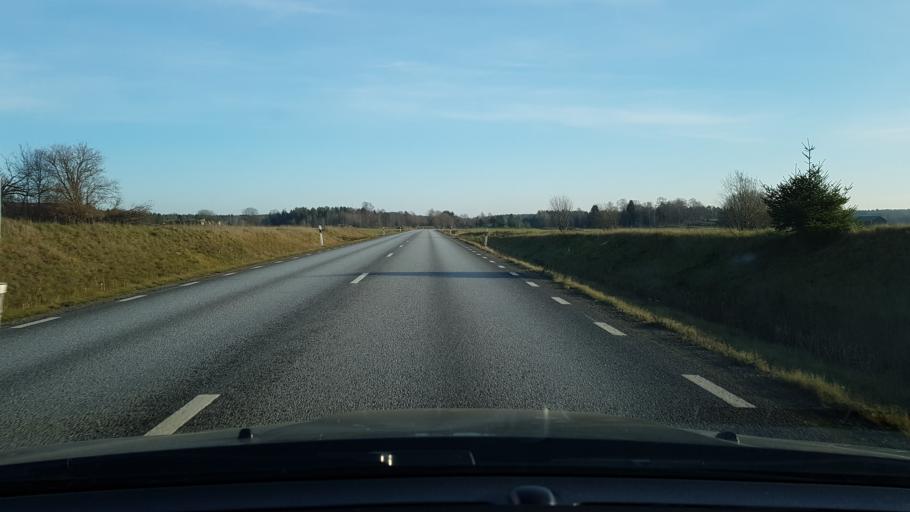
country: SE
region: Stockholm
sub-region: Vallentuna Kommun
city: Vallentuna
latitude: 59.7495
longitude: 18.0601
